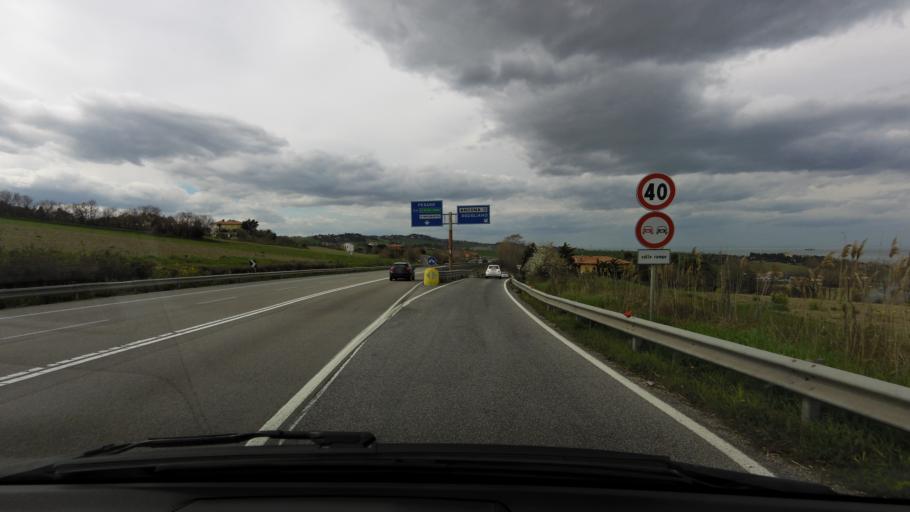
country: IT
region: The Marches
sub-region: Provincia di Ancona
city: Posatora
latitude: 43.5953
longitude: 13.4538
